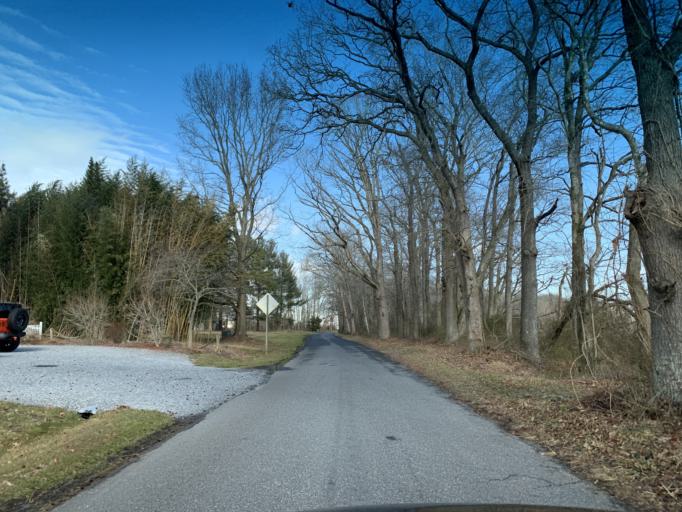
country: US
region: Delaware
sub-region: Sussex County
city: Selbyville
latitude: 38.4417
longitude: -75.1903
